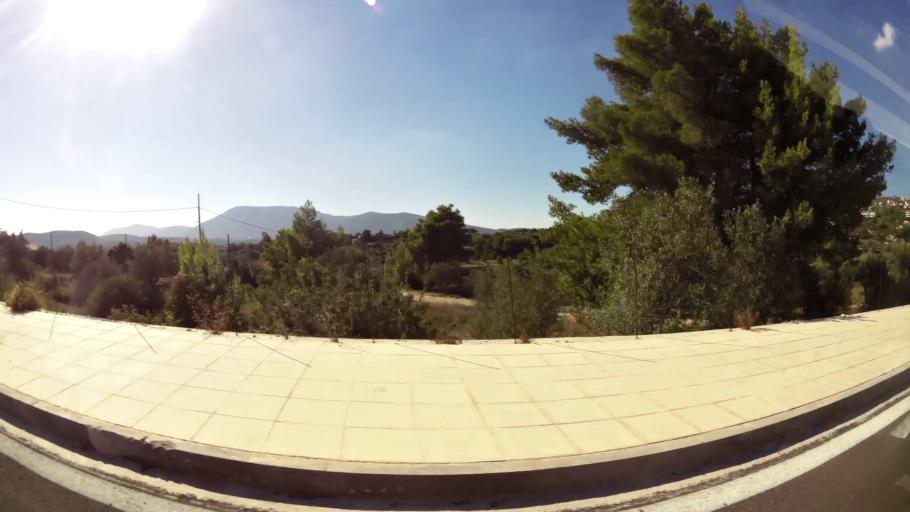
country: GR
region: Attica
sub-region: Nomarchia Anatolikis Attikis
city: Dhrafi
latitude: 38.0087
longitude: 23.9117
